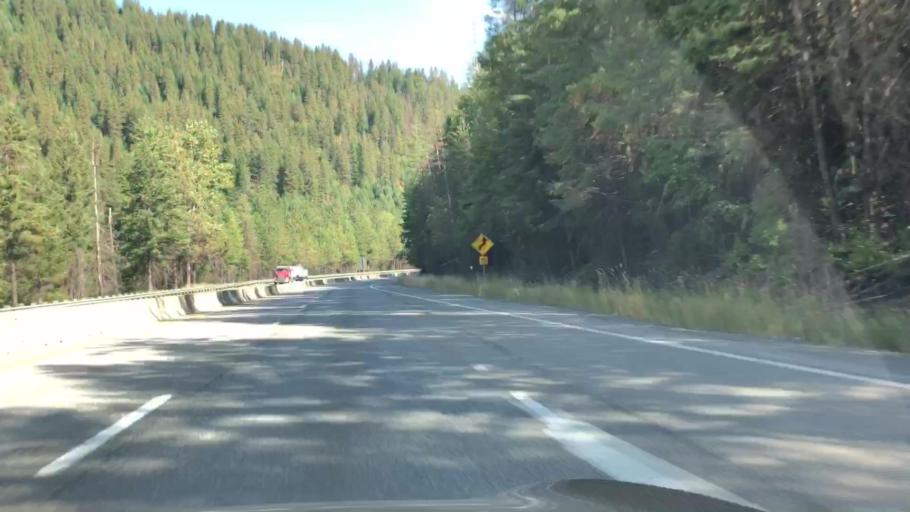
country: US
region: Idaho
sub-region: Shoshone County
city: Wallace
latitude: 47.4735
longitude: -115.8672
